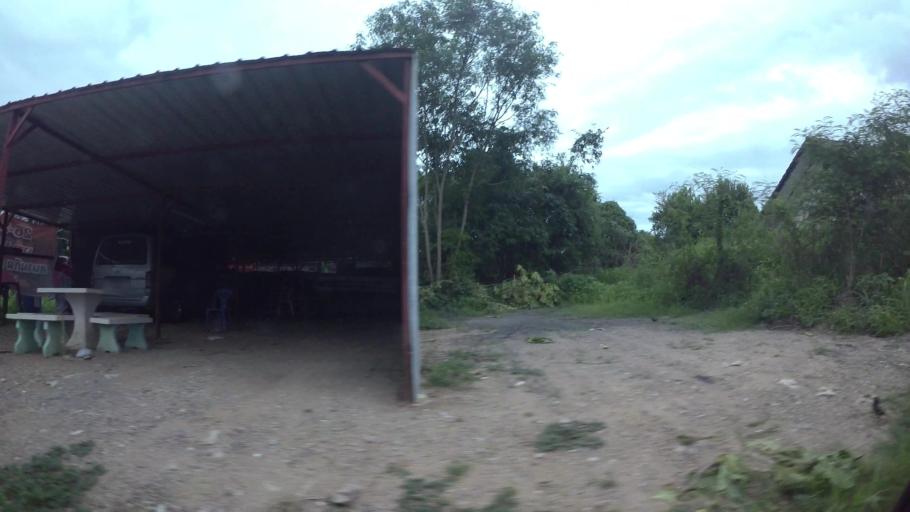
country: TH
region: Chon Buri
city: Sattahip
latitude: 12.6954
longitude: 100.8964
